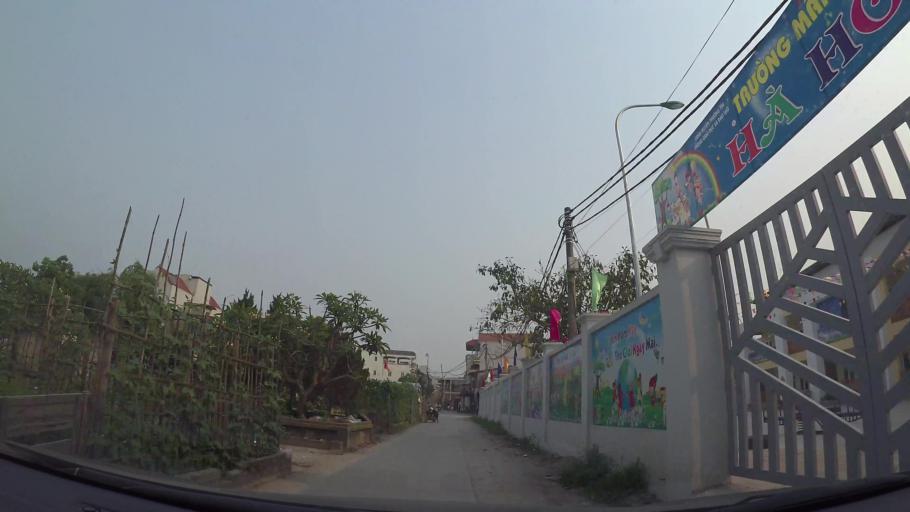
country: VN
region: Ha Noi
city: Thuong Tin
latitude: 20.8677
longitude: 105.8764
